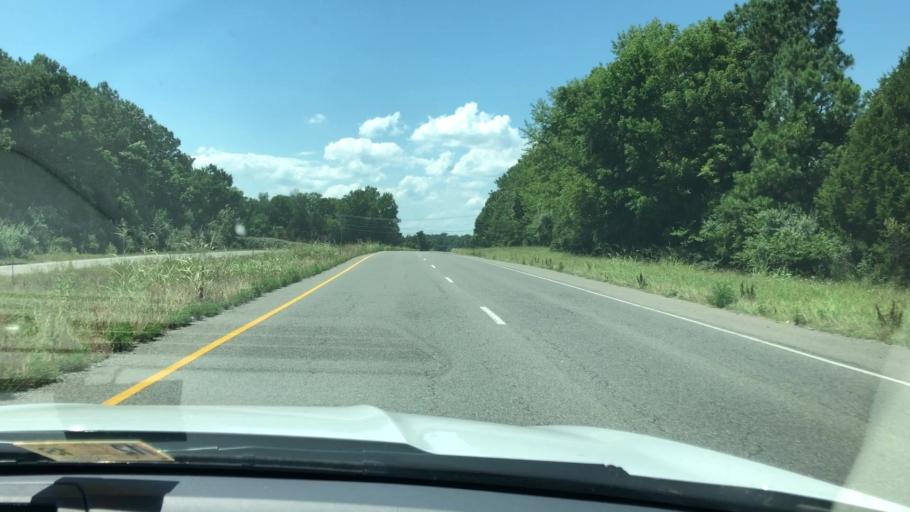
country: US
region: Virginia
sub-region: Middlesex County
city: Saluda
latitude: 37.6070
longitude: -76.5420
